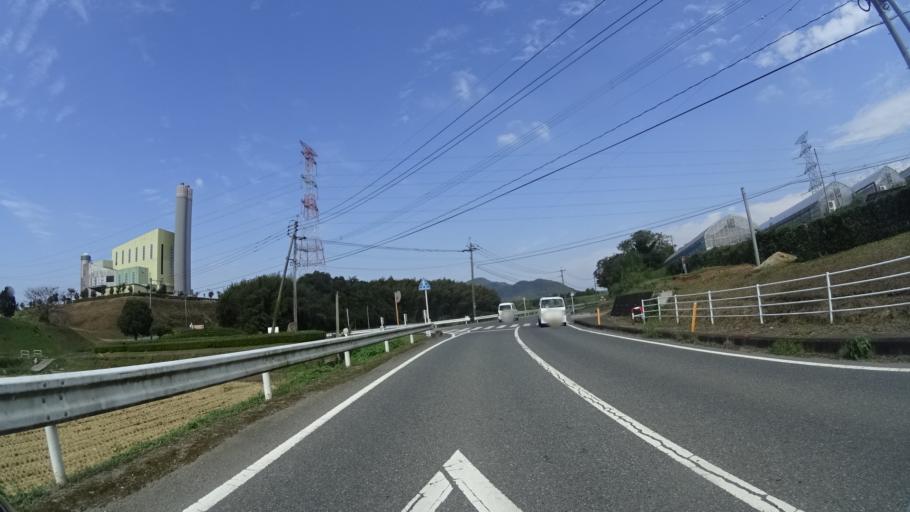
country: JP
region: Kumamoto
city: Matsubase
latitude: 32.6600
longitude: 130.7155
